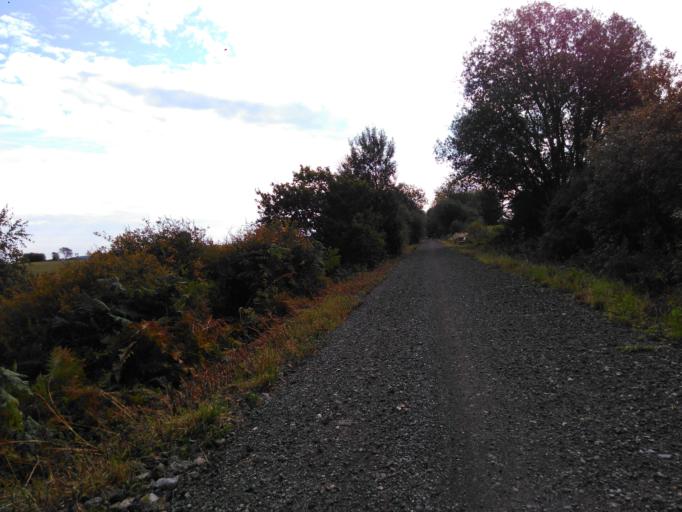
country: BE
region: Wallonia
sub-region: Province du Luxembourg
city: Neufchateau
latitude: 49.9102
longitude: 5.4456
